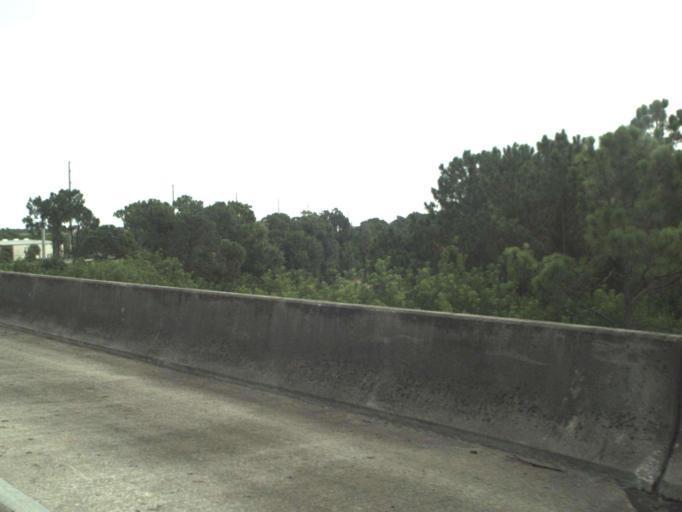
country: US
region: Florida
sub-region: Saint Lucie County
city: River Park
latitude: 27.3547
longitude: -80.4139
